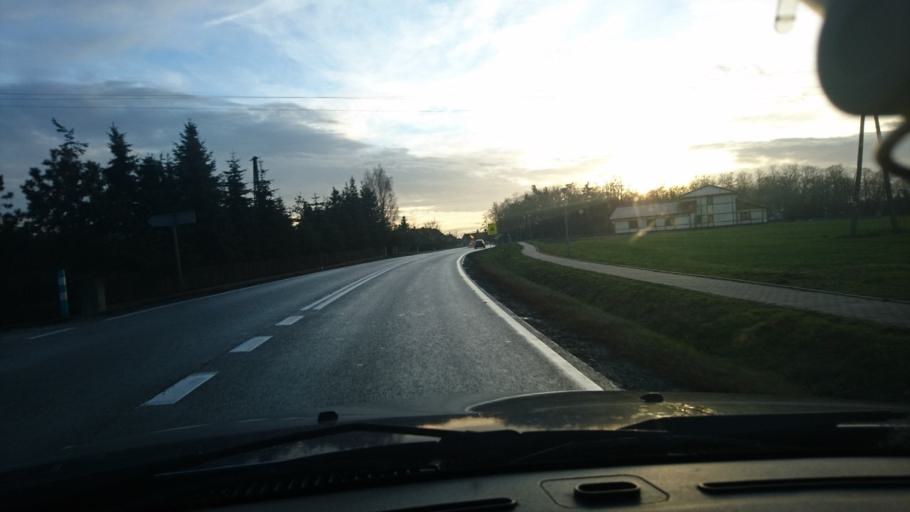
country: PL
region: Greater Poland Voivodeship
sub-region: Powiat kepinski
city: Opatow
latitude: 51.1829
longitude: 18.1461
